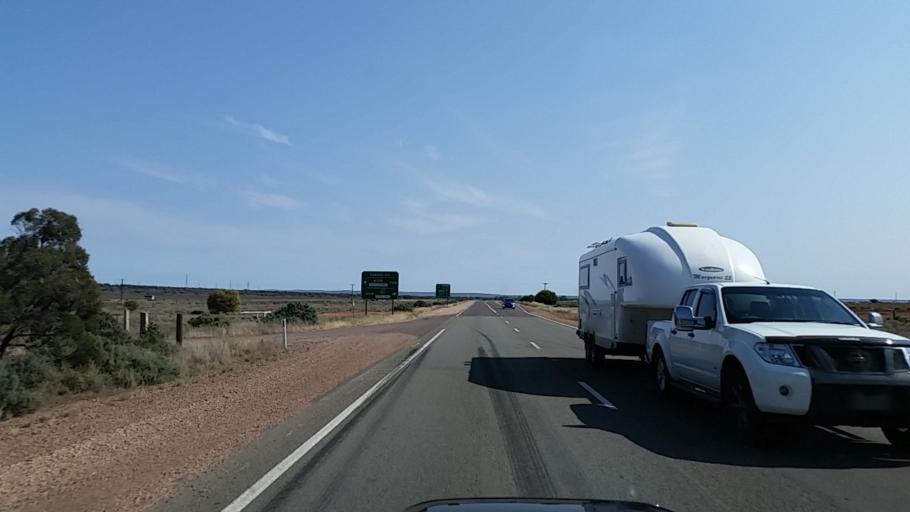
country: AU
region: South Australia
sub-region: Port Augusta
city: Port Augusta West
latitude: -32.6161
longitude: 137.5735
